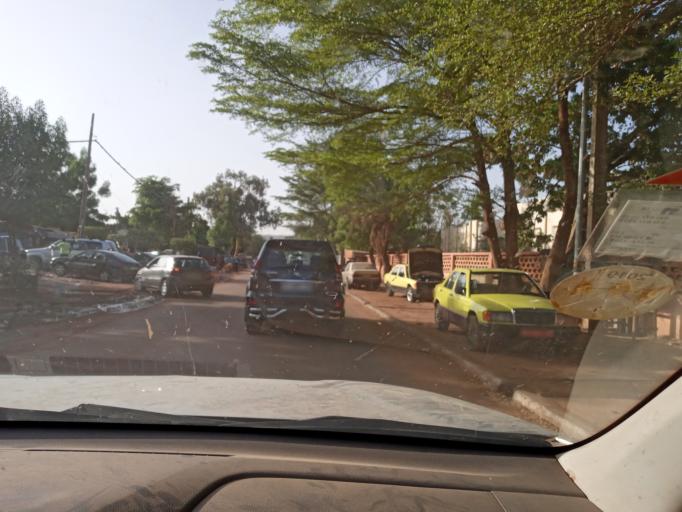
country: ML
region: Bamako
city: Bamako
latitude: 12.6576
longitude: -7.9712
